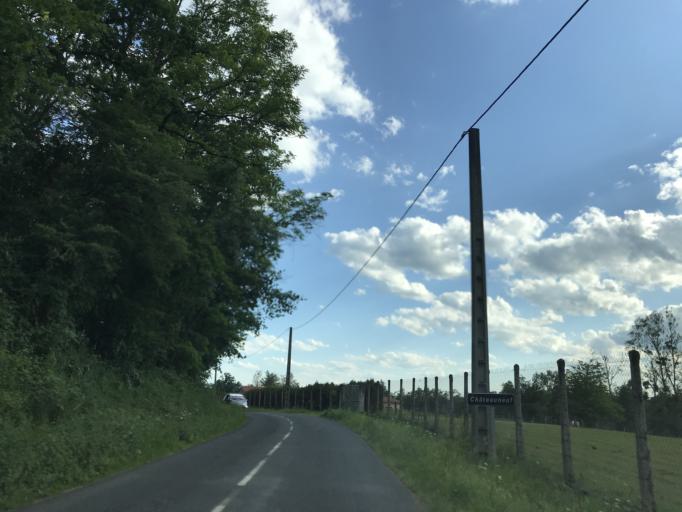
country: FR
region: Auvergne
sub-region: Departement du Puy-de-Dome
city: Courpiere
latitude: 45.7679
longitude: 3.6012
